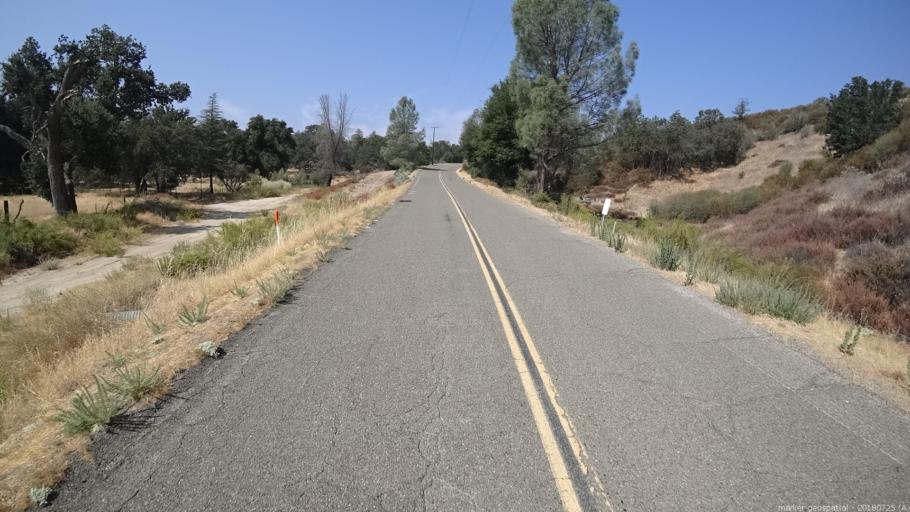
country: US
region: California
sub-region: San Luis Obispo County
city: San Miguel
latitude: 35.9250
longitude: -120.5088
